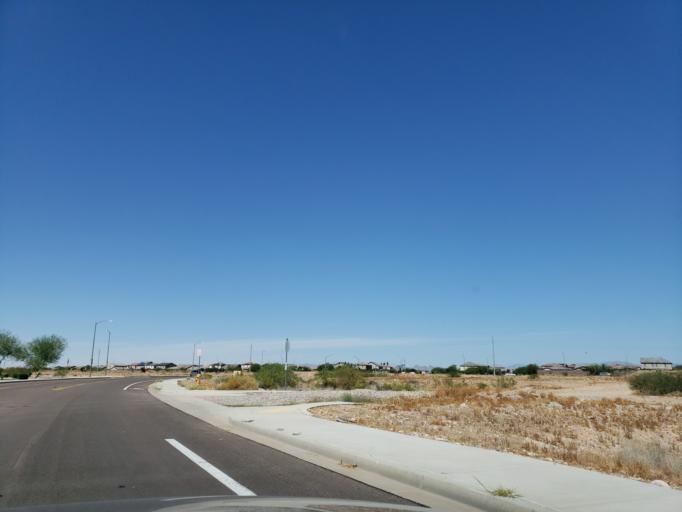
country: US
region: Arizona
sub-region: Maricopa County
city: Sun City West
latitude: 33.6793
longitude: -112.2687
